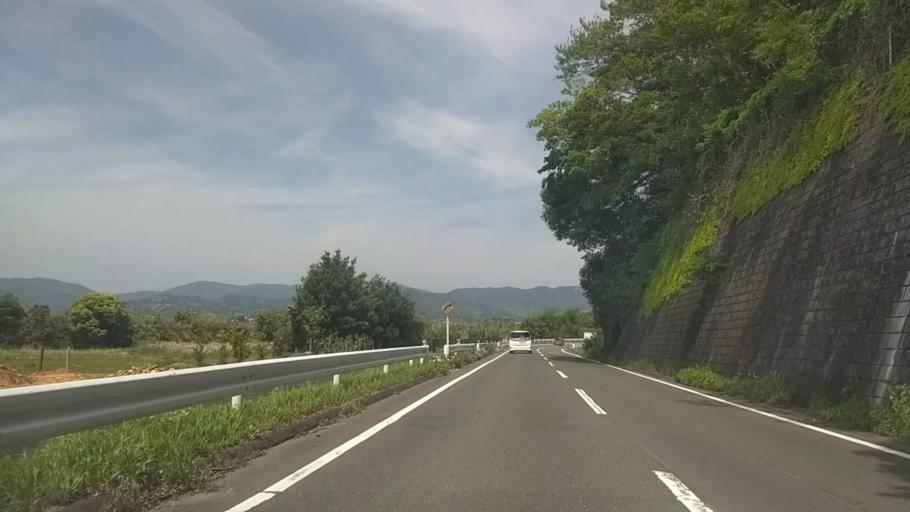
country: JP
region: Shizuoka
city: Kosai-shi
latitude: 34.7700
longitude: 137.5555
